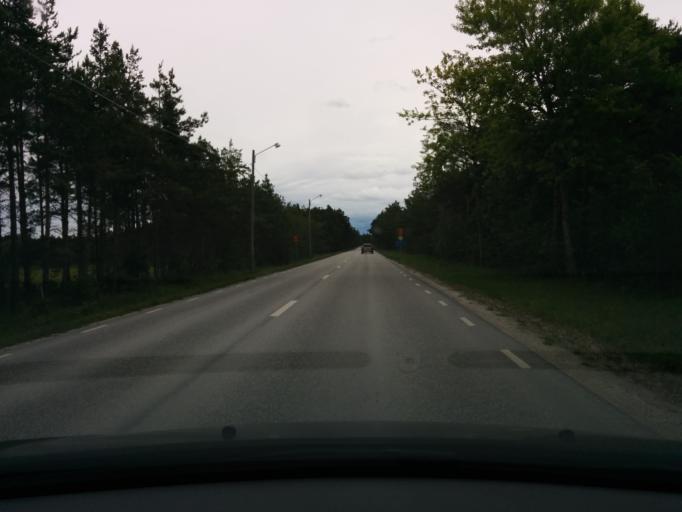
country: SE
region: Gotland
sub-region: Gotland
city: Slite
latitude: 57.6813
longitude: 18.7683
